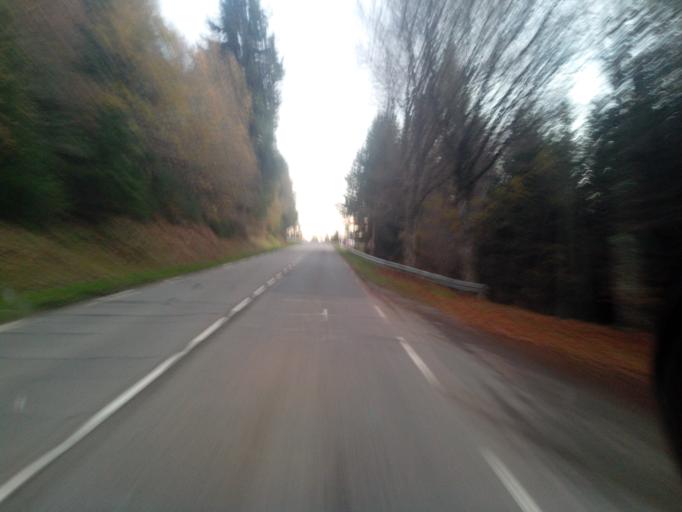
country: FR
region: Limousin
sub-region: Departement de la Correze
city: Meymac
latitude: 45.5265
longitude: 2.1601
